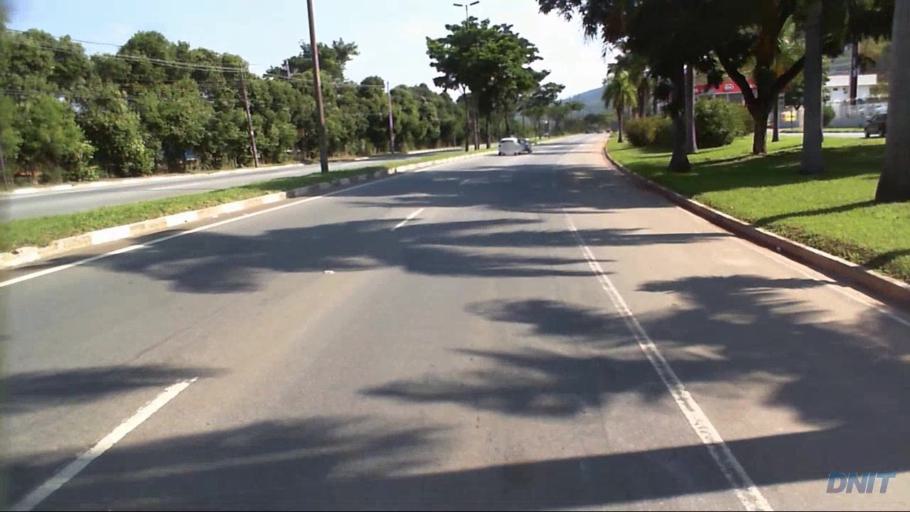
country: BR
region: Minas Gerais
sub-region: Ipatinga
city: Ipatinga
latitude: -19.4815
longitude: -42.5460
